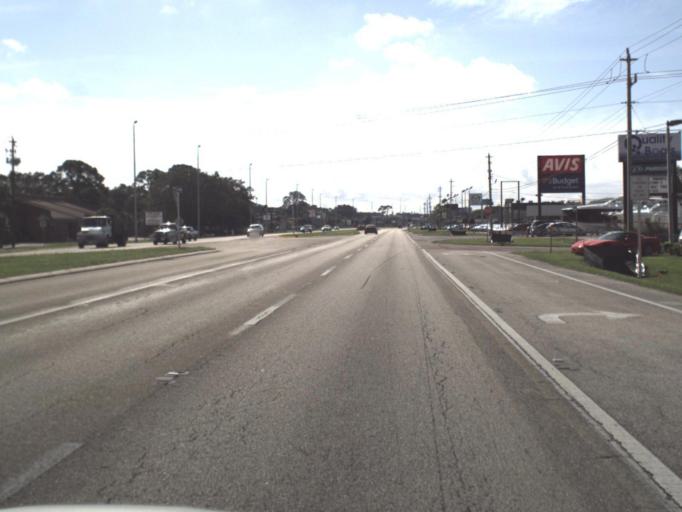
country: US
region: Florida
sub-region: Sarasota County
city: Gulf Gate Estates
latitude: 27.2552
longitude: -82.5179
